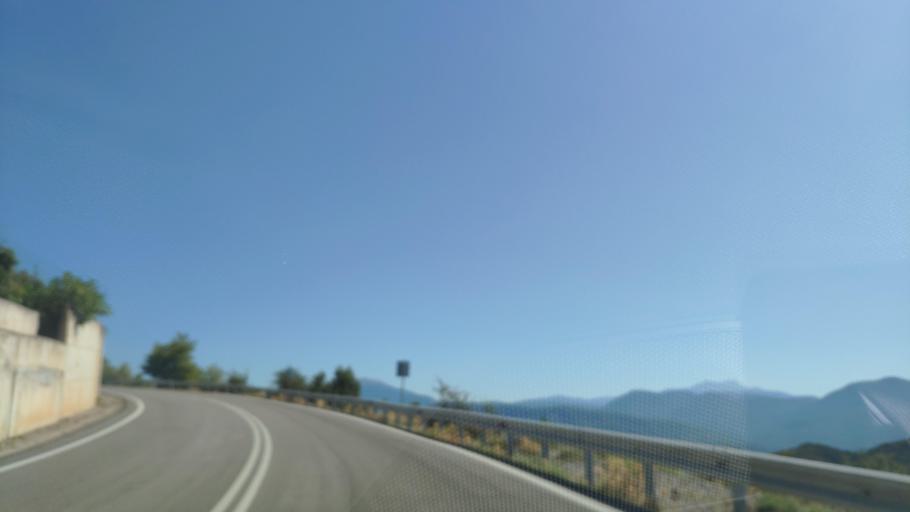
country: GR
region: Central Greece
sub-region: Nomos Evrytanias
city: Kerasochori
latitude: 38.9304
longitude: 21.4462
